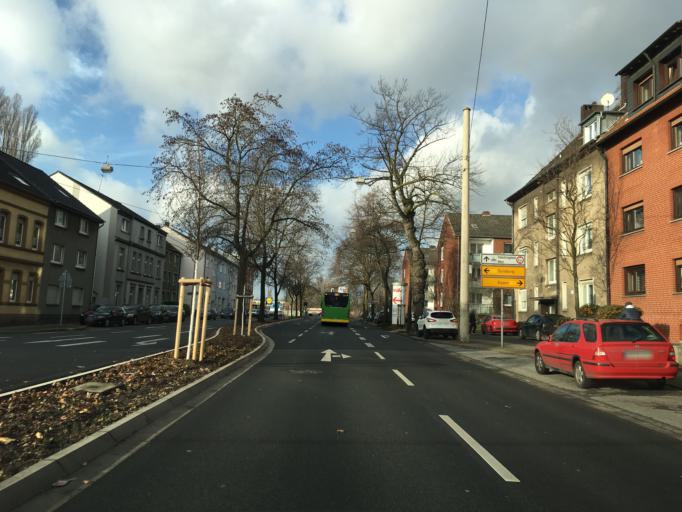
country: DE
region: North Rhine-Westphalia
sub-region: Regierungsbezirk Dusseldorf
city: Oberhausen
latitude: 51.4768
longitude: 6.8419
